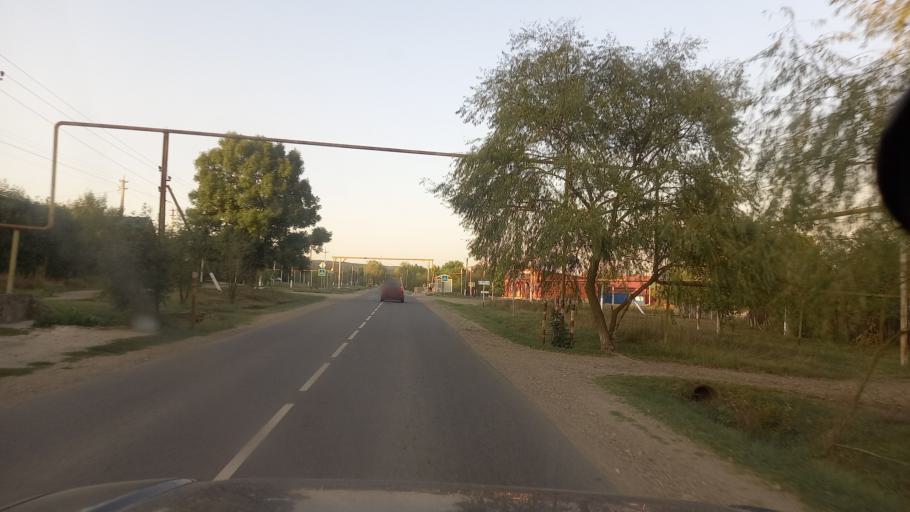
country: RU
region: Krasnodarskiy
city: Smolenskaya
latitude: 44.7721
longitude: 38.7843
